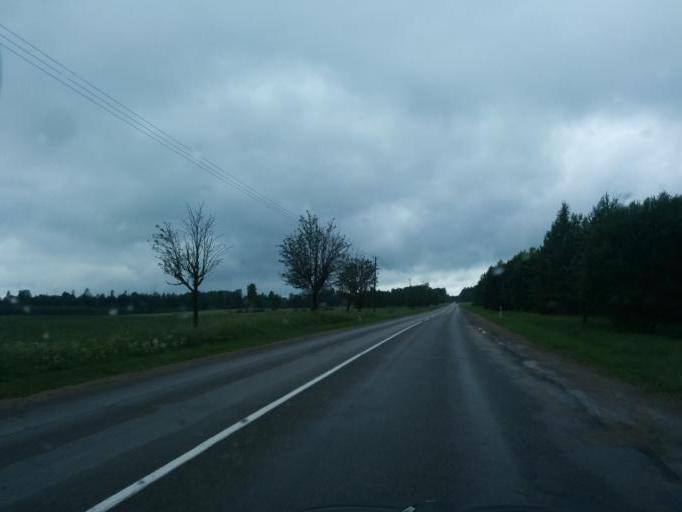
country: LV
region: Smiltene
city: Smiltene
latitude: 57.3919
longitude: 25.9705
